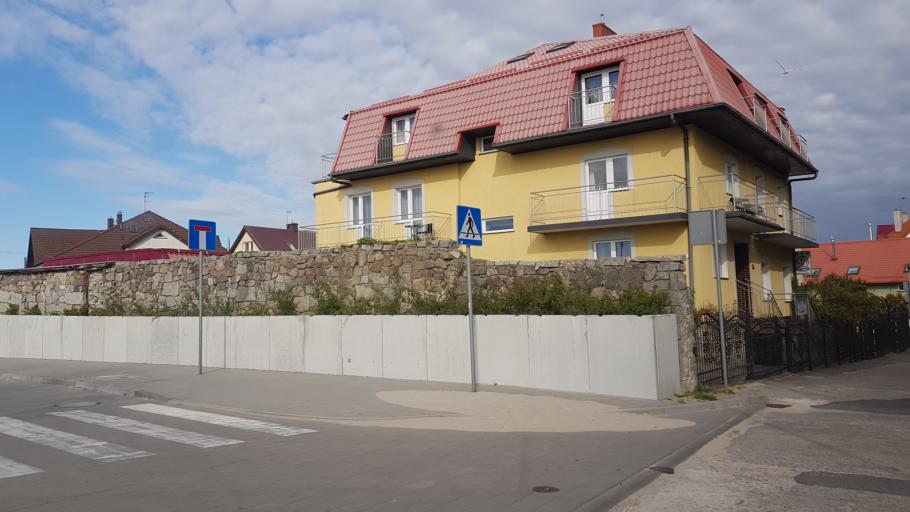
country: PL
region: West Pomeranian Voivodeship
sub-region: Powiat slawienski
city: Darlowo
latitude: 54.4383
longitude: 16.3758
